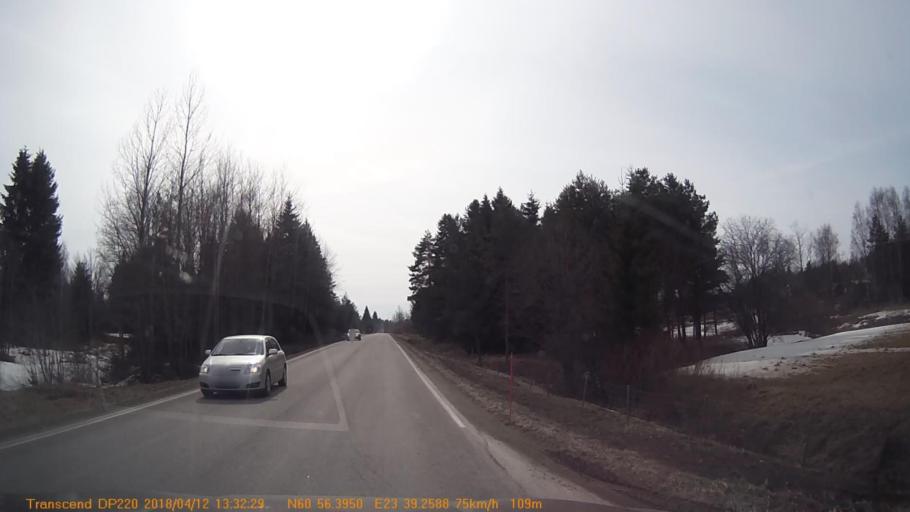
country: FI
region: Haeme
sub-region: Forssa
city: Forssa
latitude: 60.9398
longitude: 23.6542
